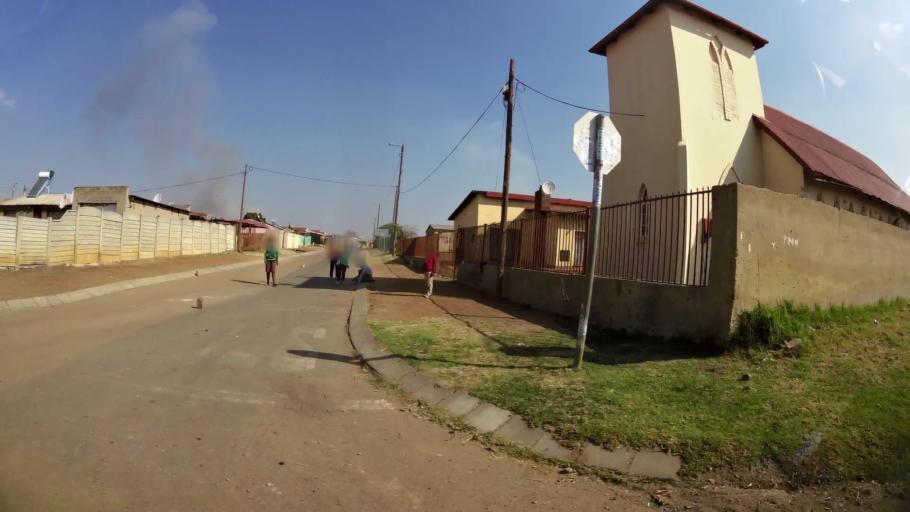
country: ZA
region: Gauteng
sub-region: Ekurhuleni Metropolitan Municipality
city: Brakpan
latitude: -26.1436
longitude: 28.4162
